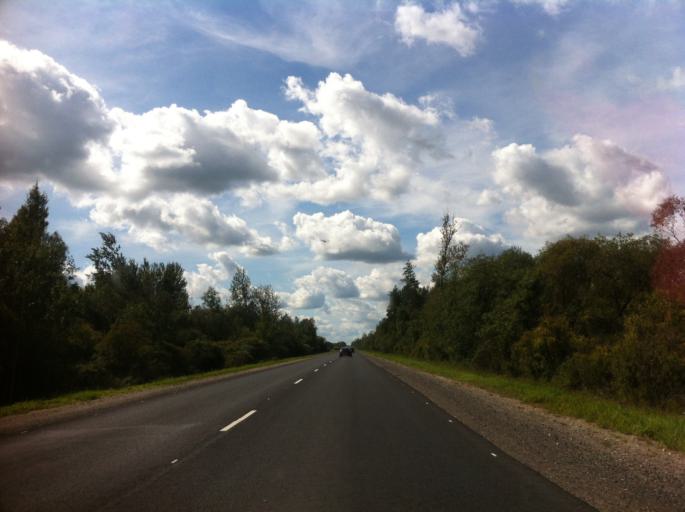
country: RU
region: Pskov
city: Izborsk
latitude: 57.7441
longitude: 28.0249
